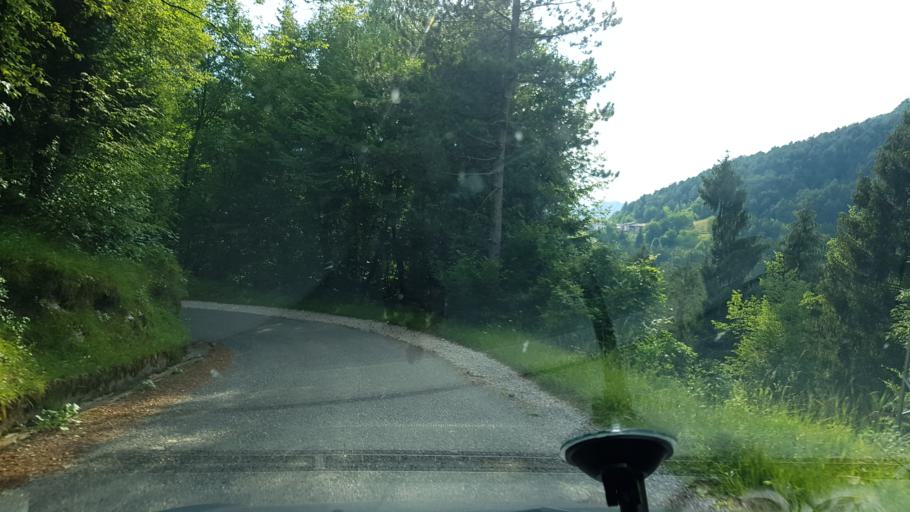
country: IT
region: Friuli Venezia Giulia
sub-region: Provincia di Udine
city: Prato
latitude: 46.3585
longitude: 13.3679
